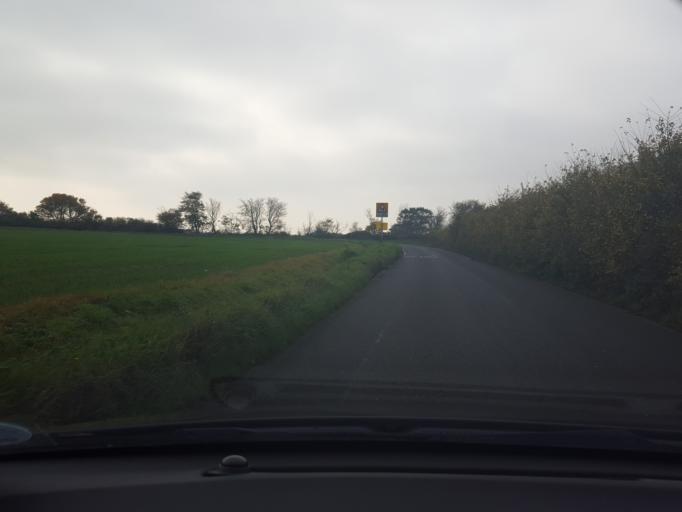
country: GB
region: England
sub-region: Essex
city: Saint Osyth
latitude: 51.7908
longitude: 1.0850
